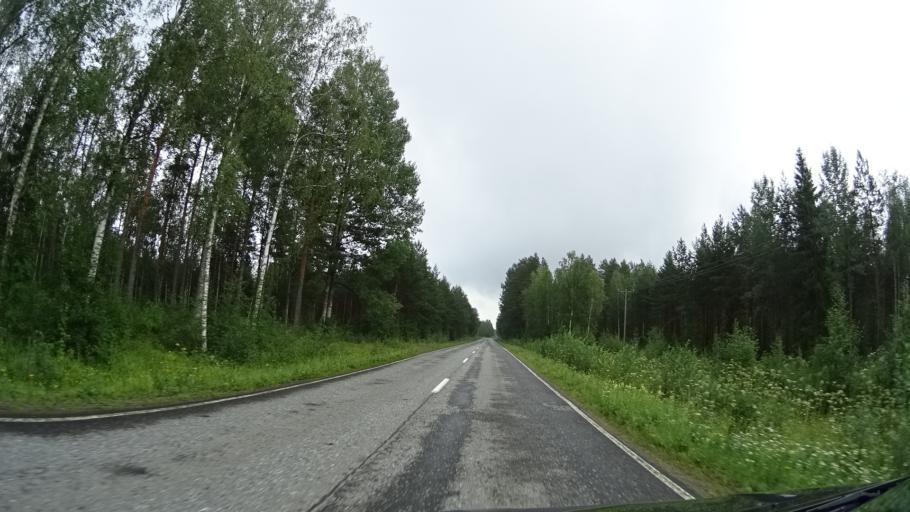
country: FI
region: North Karelia
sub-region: Keski-Karjala
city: Raeaekkylae
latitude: 62.3101
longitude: 29.5252
